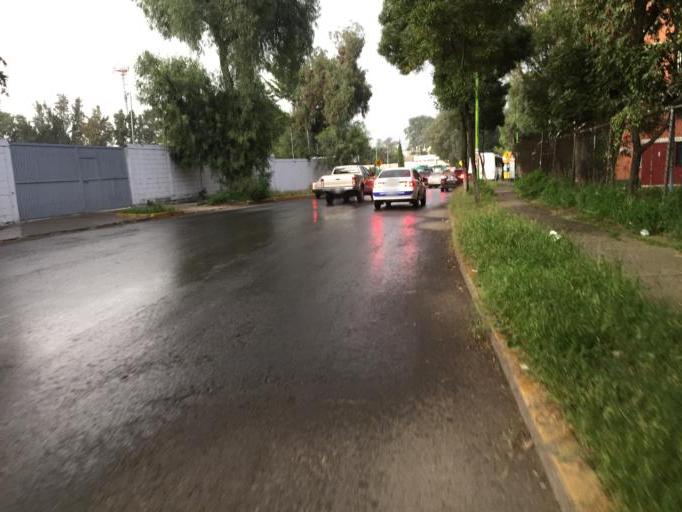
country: MX
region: Mexico
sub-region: Cuautitlan Izcalli
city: Axotlan
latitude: 19.6761
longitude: -99.2141
